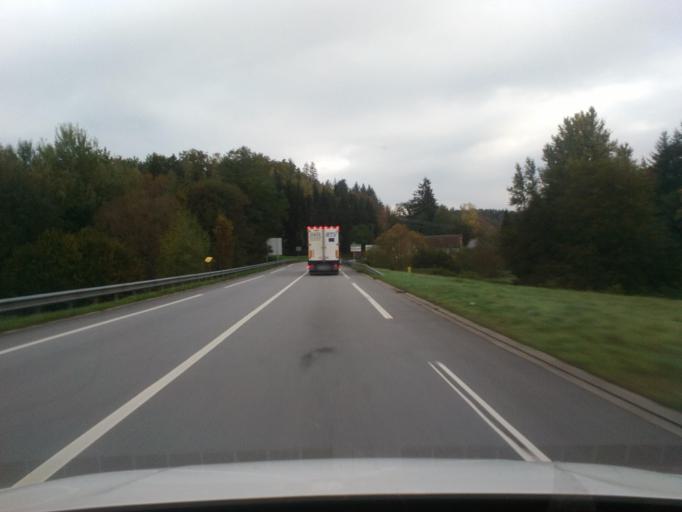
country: FR
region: Lorraine
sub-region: Departement des Vosges
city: Ban-de-Laveline
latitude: 48.2945
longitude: 7.0719
